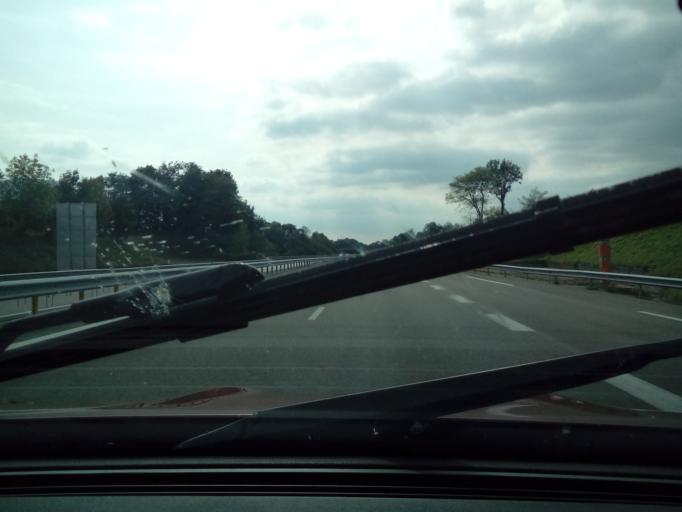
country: FR
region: Rhone-Alpes
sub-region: Departement de l'Isere
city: Vinay
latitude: 45.1970
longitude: 5.4208
